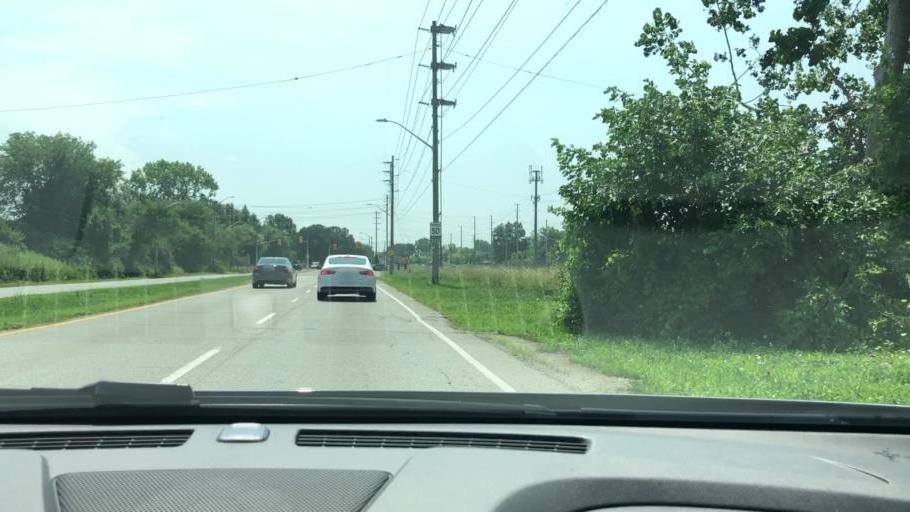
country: US
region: Michigan
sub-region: Wayne County
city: River Rouge
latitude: 42.2514
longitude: -83.0897
